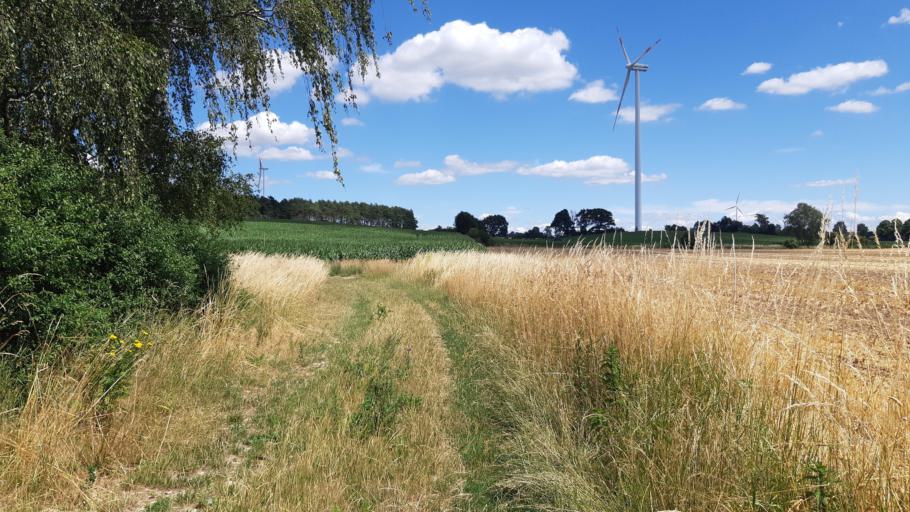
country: DE
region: Lower Saxony
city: Dahlem
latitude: 53.1941
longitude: 10.7721
